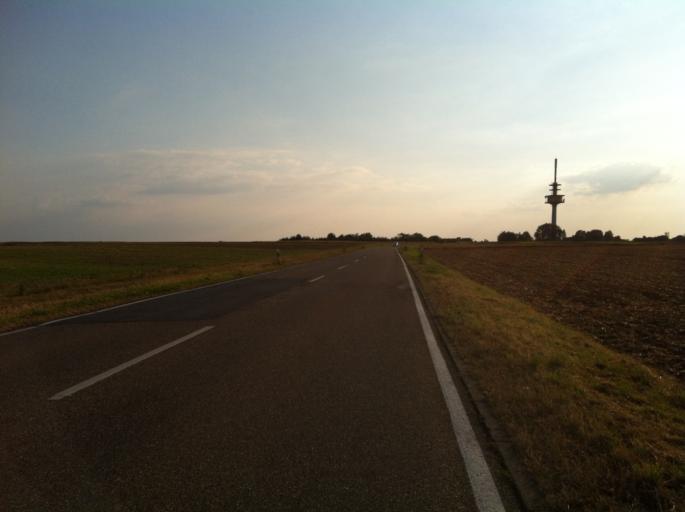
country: DE
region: Rheinland-Pfalz
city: Ober-Olm
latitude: 49.9463
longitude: 8.1817
